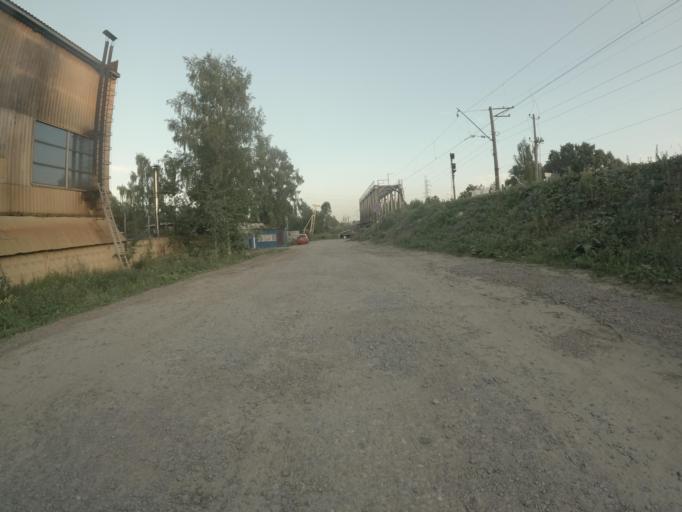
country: RU
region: St.-Petersburg
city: Krasnogvargeisky
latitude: 59.9422
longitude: 30.4480
